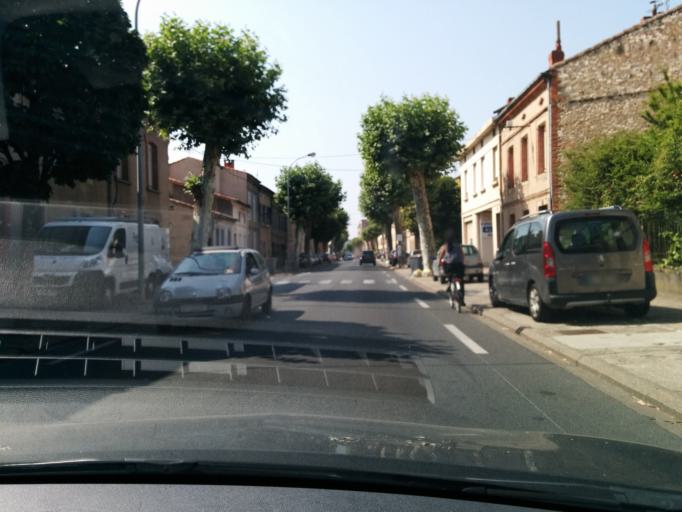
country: FR
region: Midi-Pyrenees
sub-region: Departement du Tarn
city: Albi
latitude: 43.9362
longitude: 2.1452
